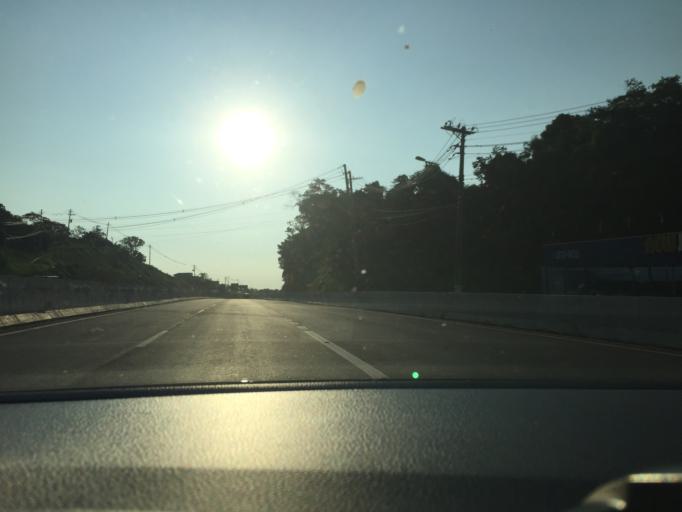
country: BR
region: Sao Paulo
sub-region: Louveira
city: Louveira
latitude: -23.0909
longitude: -46.9525
